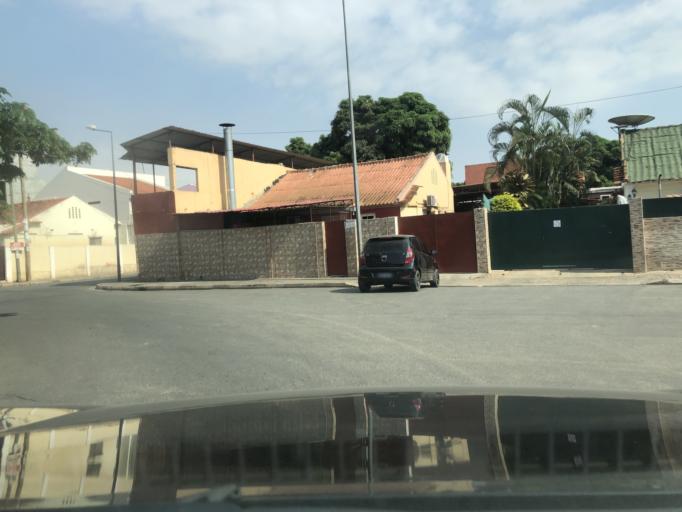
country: AO
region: Luanda
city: Luanda
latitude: -8.8264
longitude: 13.2496
